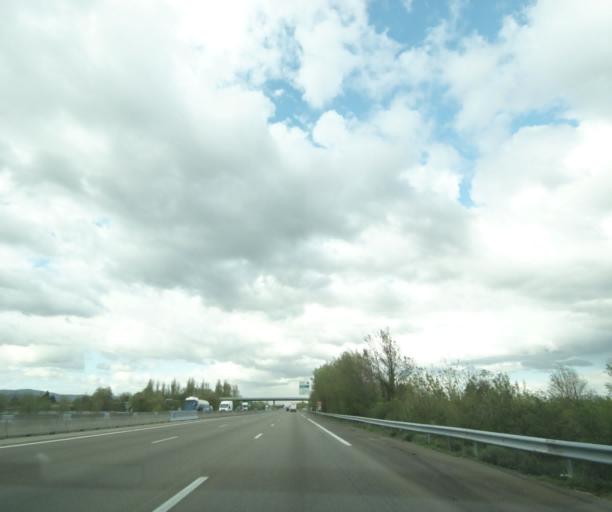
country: FR
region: Rhone-Alpes
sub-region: Departement de la Drome
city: Loriol-sur-Drome
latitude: 44.7561
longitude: 4.7934
